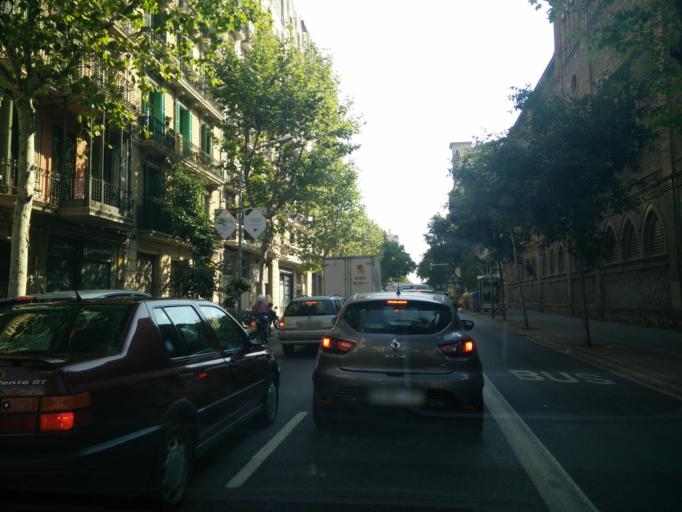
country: ES
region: Catalonia
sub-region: Provincia de Barcelona
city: Eixample
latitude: 41.3987
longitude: 2.1713
